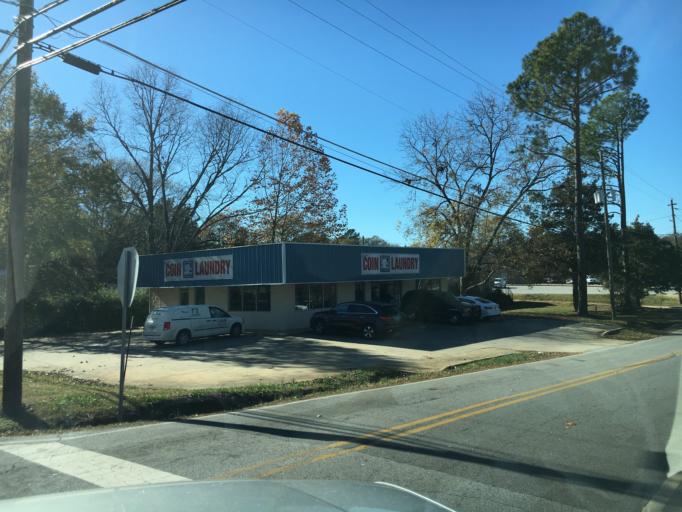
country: US
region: Georgia
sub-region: Hart County
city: Hartwell
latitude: 34.3454
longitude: -82.9378
